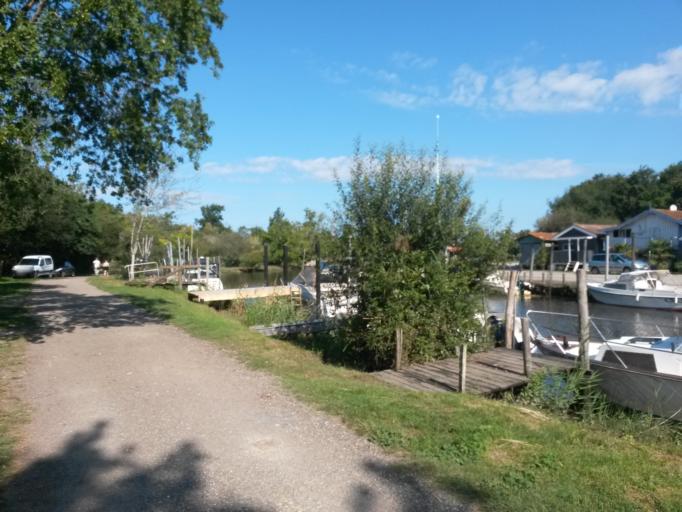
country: FR
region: Aquitaine
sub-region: Departement de la Gironde
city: Le Teich
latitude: 44.6435
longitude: -0.9995
